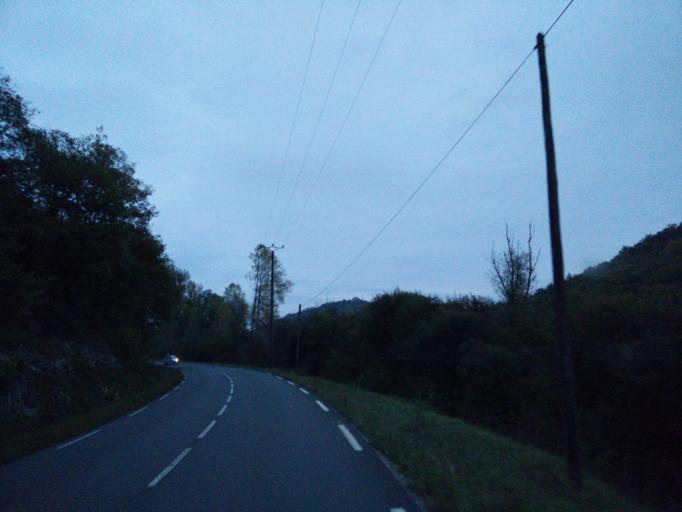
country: FR
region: Aquitaine
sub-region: Departement de la Dordogne
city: Saint-Cyprien
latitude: 44.9250
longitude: 1.0819
